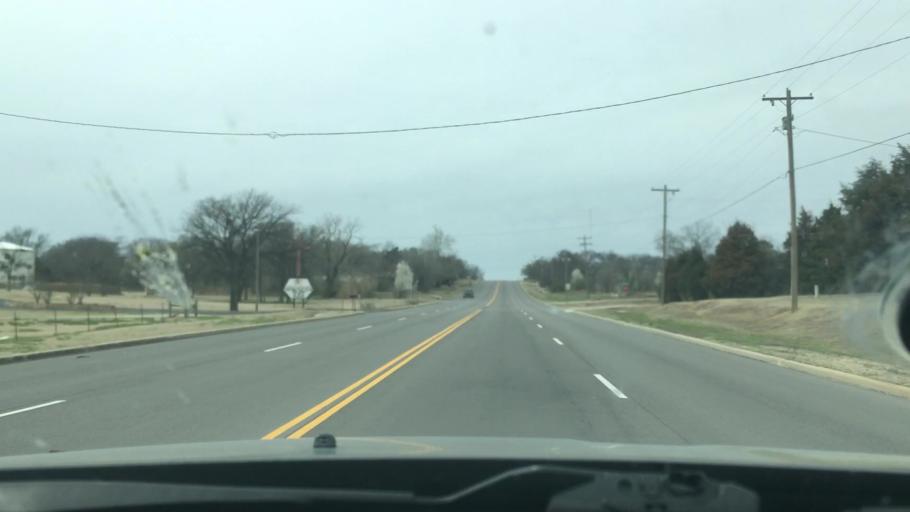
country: US
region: Oklahoma
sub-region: Seminole County
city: Seminole
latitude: 35.2527
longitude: -96.7058
